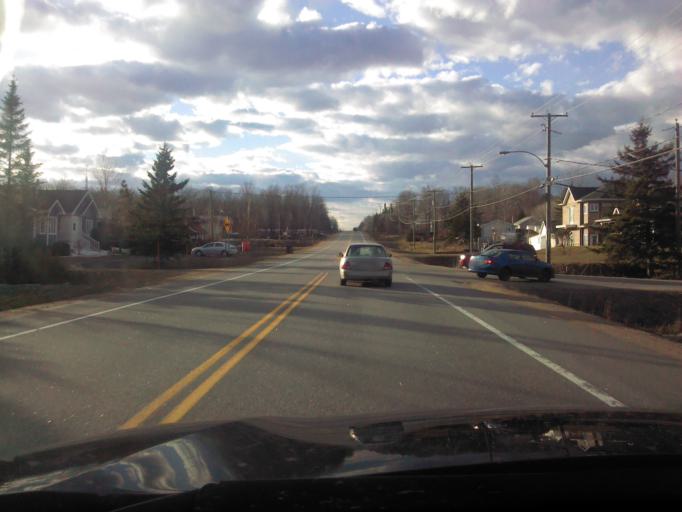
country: CA
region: Quebec
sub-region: Capitale-Nationale
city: Sainte Catherine de la Jacques Cartier
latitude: 46.7988
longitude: -71.5511
